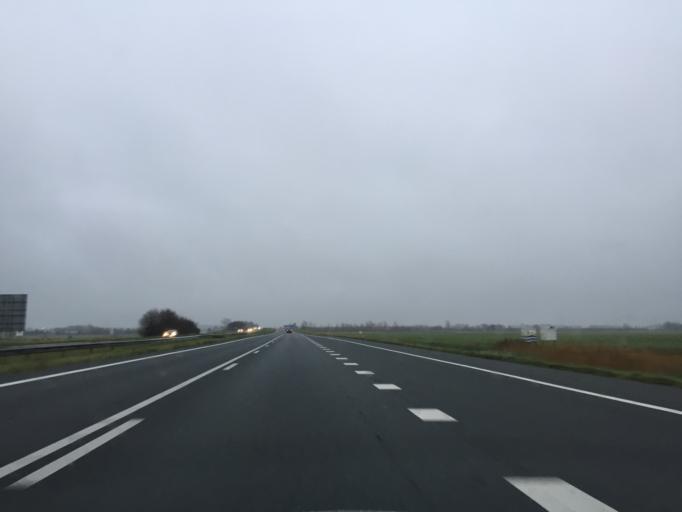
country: NL
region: Zeeland
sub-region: Gemeente Goes
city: Goes
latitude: 51.4808
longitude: 3.8868
